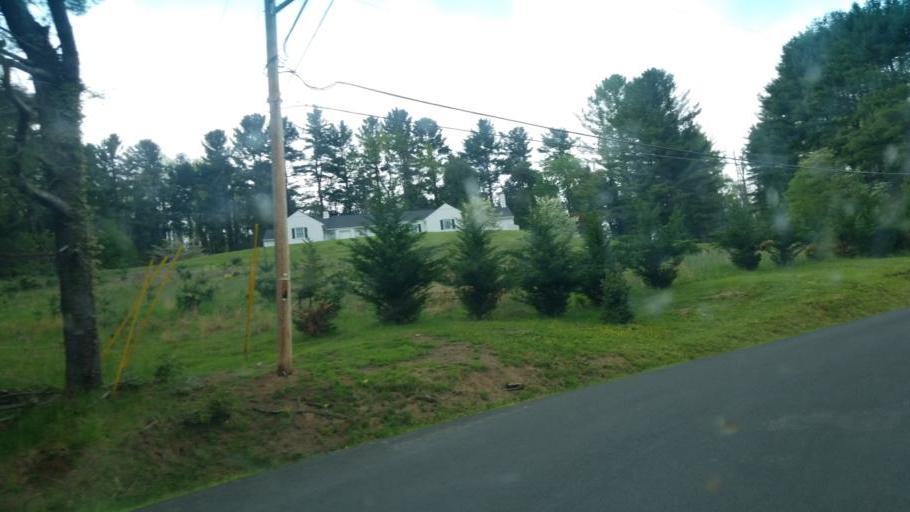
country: US
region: Virginia
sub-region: Smyth County
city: Marion
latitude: 36.8509
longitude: -81.4971
